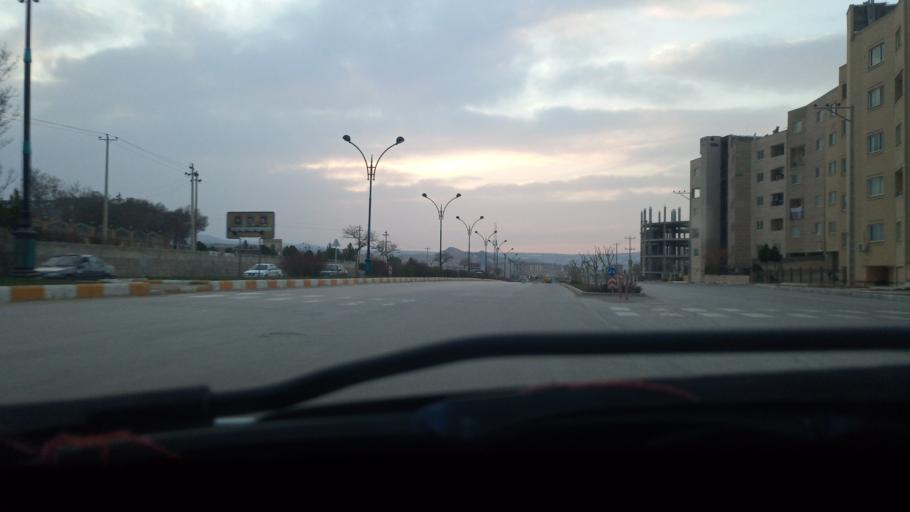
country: IR
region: Khorasan-e Shomali
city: Bojnurd
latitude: 37.4544
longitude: 57.3249
